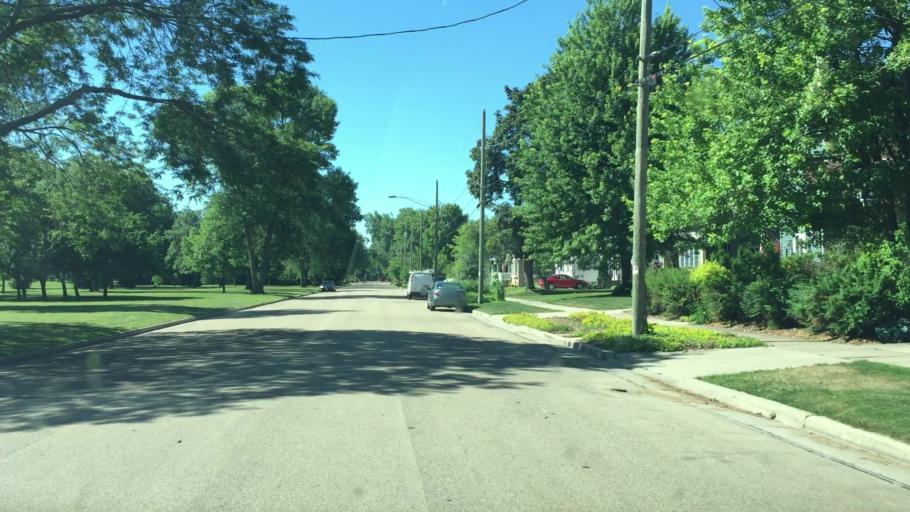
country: US
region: Wisconsin
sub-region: Winnebago County
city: Menasha
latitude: 44.1964
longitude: -88.4421
